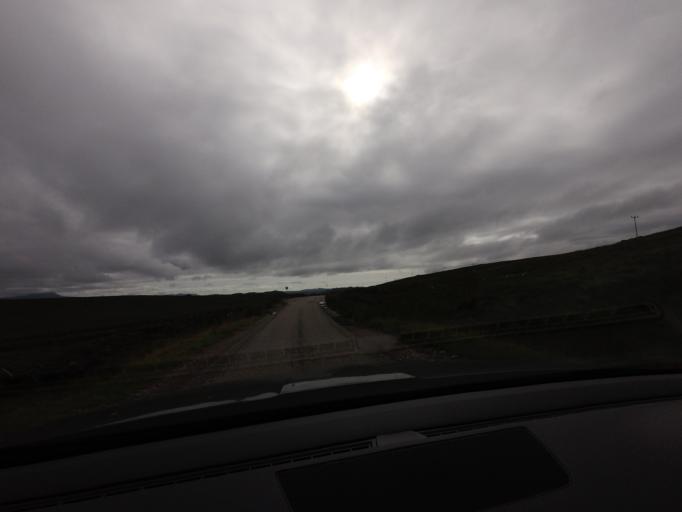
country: GB
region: Scotland
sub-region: Highland
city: Ullapool
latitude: 58.4537
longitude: -4.9306
